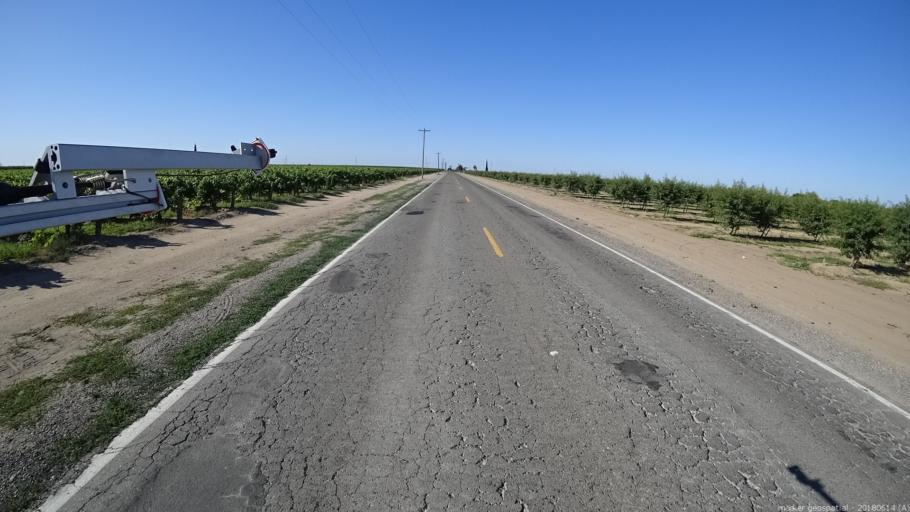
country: US
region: California
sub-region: Madera County
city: Madera
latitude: 36.9280
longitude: -120.1286
